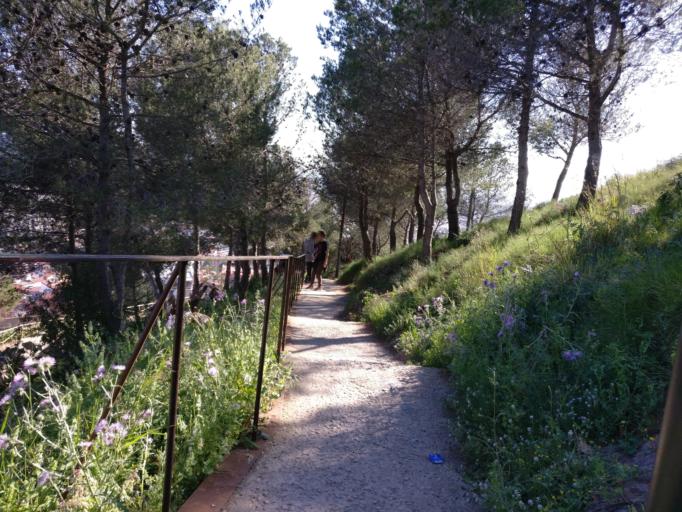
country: ES
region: Catalonia
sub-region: Provincia de Barcelona
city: Horta-Guinardo
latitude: 41.4187
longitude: 2.1614
